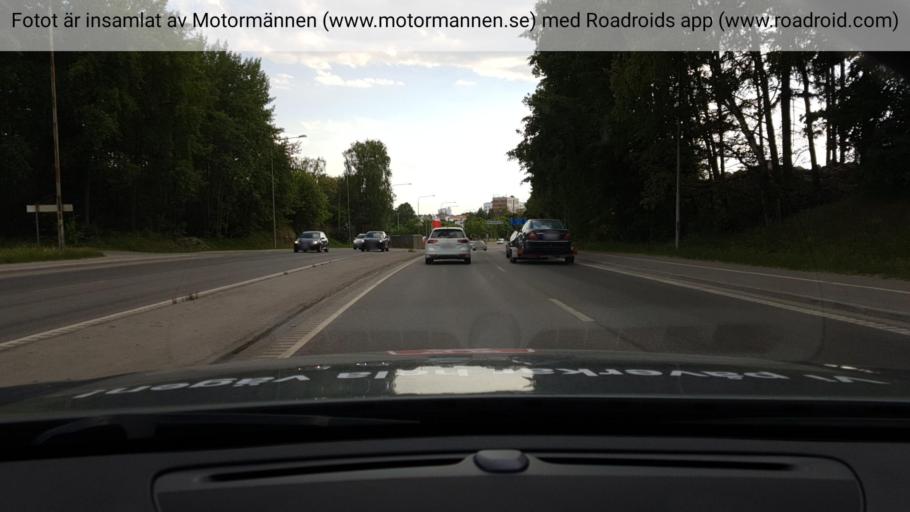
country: SE
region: Stockholm
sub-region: Huddinge Kommun
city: Huddinge
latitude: 59.2470
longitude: 18.0033
